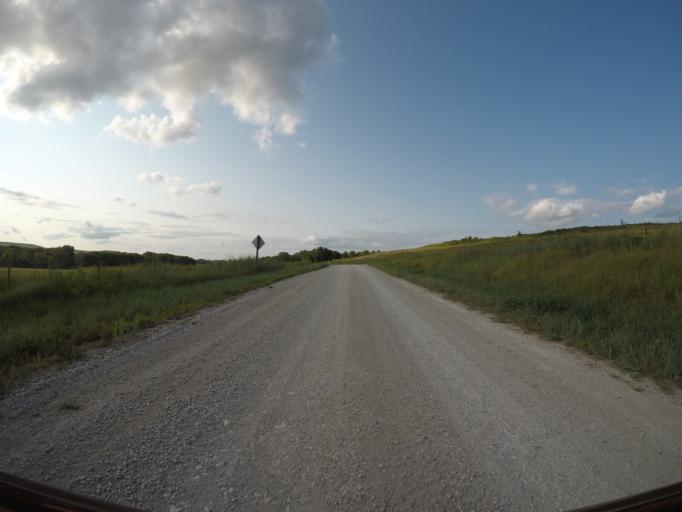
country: US
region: Kansas
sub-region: Wabaunsee County
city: Alma
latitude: 38.8961
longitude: -96.2060
